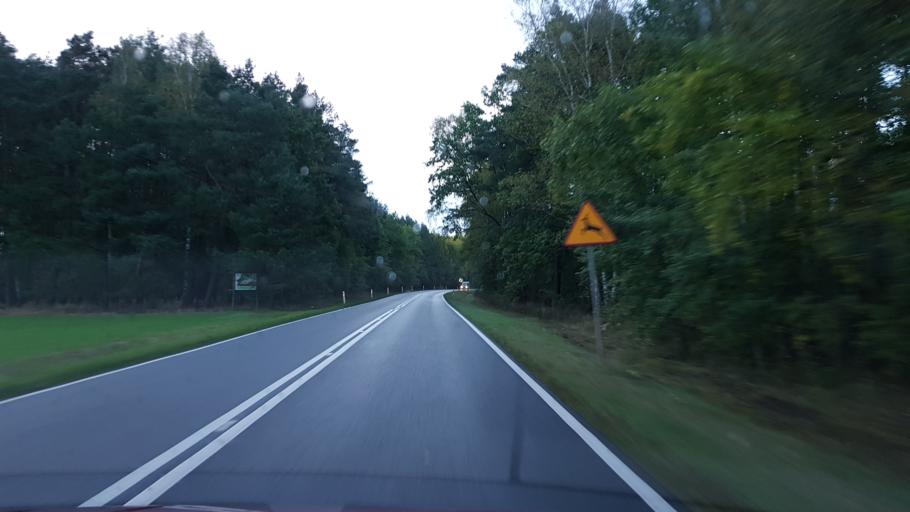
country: PL
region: Greater Poland Voivodeship
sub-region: Powiat zlotowski
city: Krajenka
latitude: 53.2781
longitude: 16.9547
